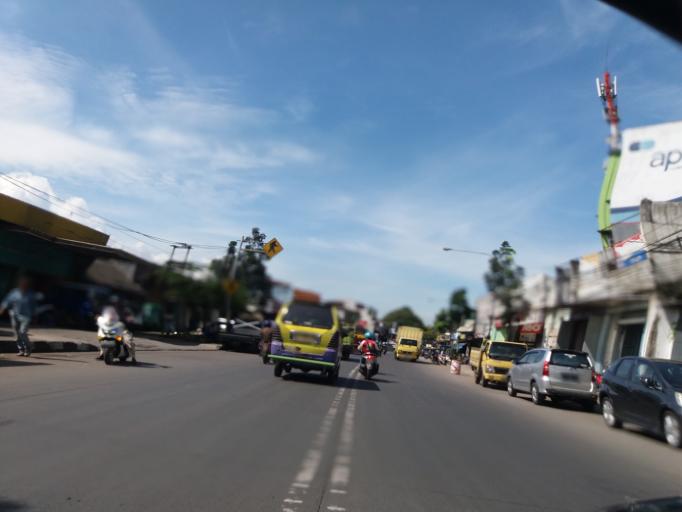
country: ID
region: West Java
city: Bandung
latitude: -6.9260
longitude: 107.5876
